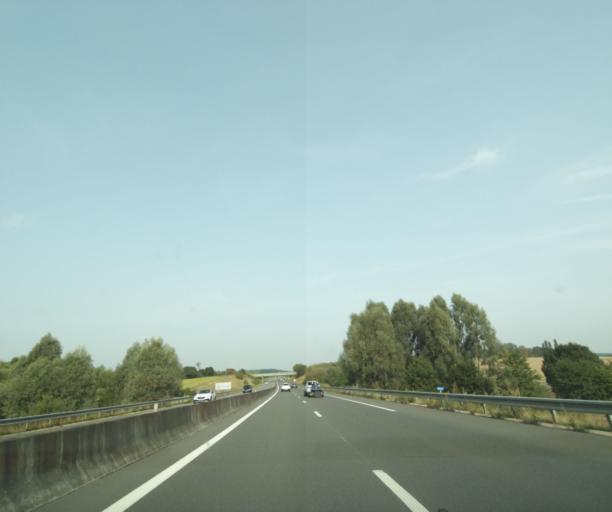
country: FR
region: Pays de la Loire
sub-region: Departement de la Sarthe
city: Champfleur
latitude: 48.3212
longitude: 0.1267
